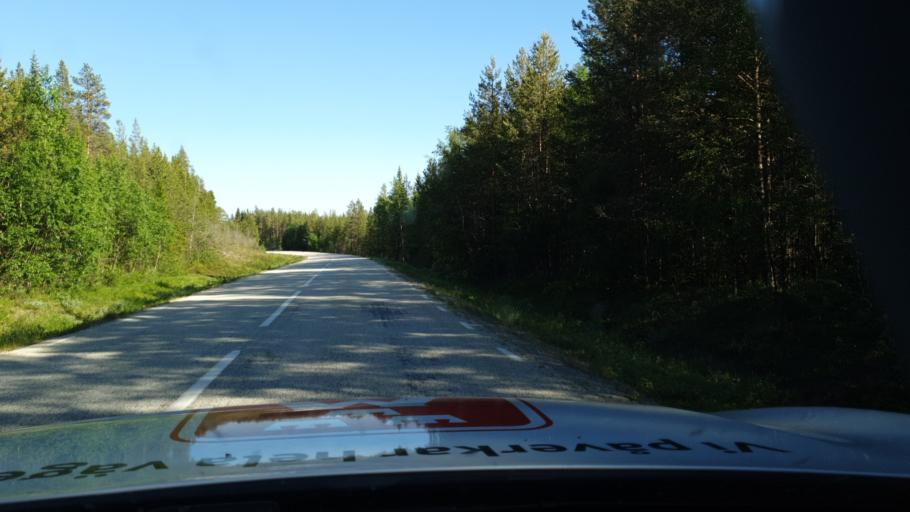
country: SE
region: Jaemtland
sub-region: Are Kommun
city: Jarpen
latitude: 62.8188
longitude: 13.5084
